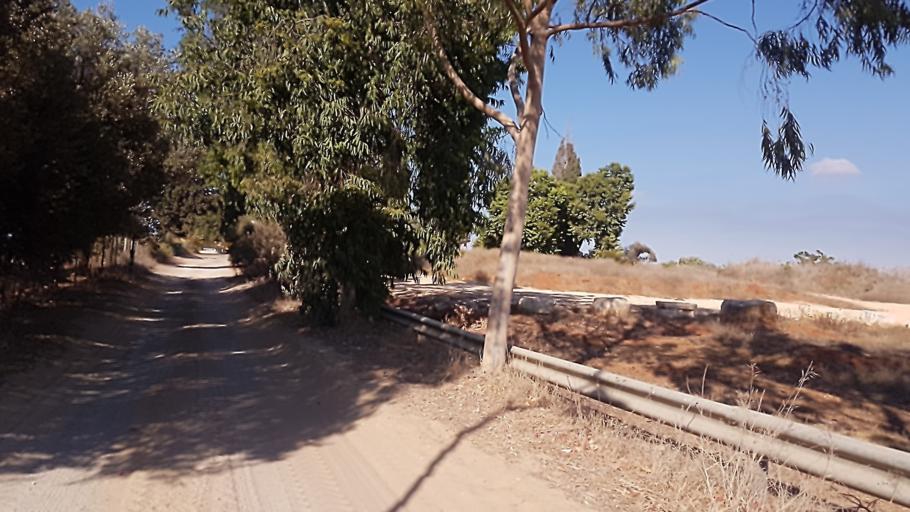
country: IL
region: Central District
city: Kfar Saba
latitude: 32.2034
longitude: 34.9146
